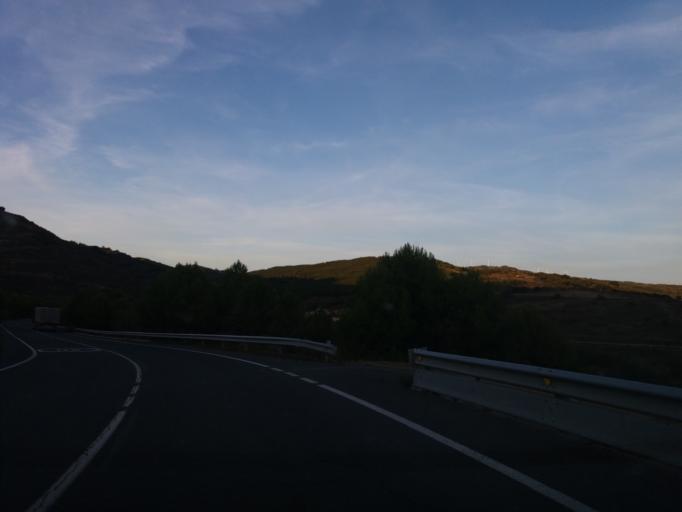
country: ES
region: Navarre
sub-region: Provincia de Navarra
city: San Martin de Unx
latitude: 42.5257
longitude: -1.5566
